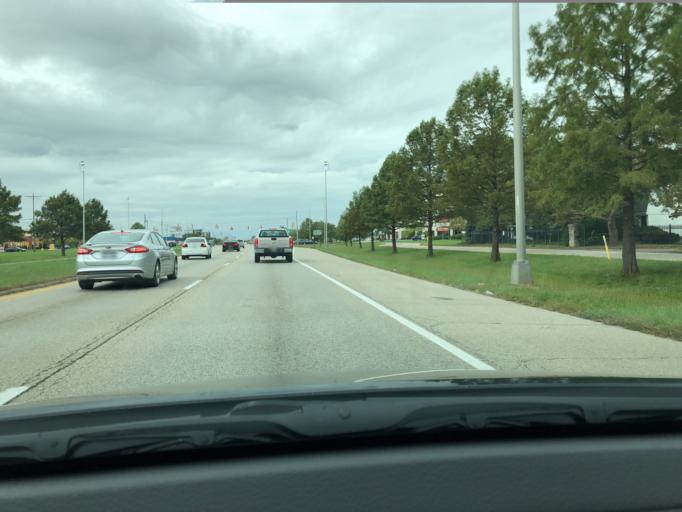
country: US
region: Ohio
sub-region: Franklin County
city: Minerva Park
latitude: 40.0835
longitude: -82.9434
